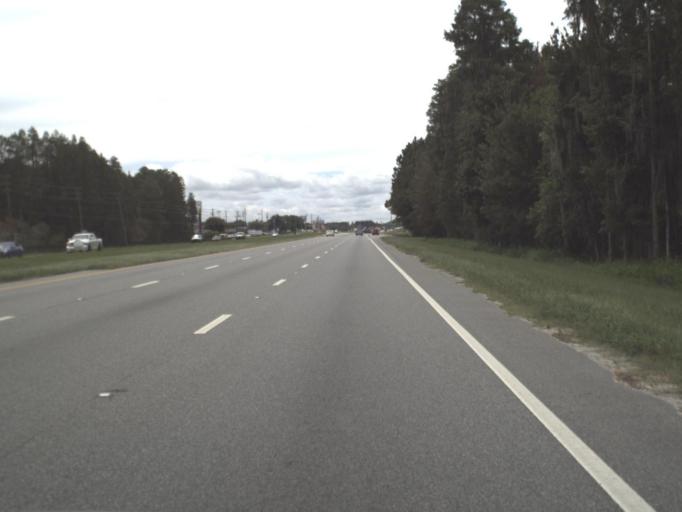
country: US
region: Florida
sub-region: Pasco County
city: Land O' Lakes
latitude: 28.1862
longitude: -82.4301
